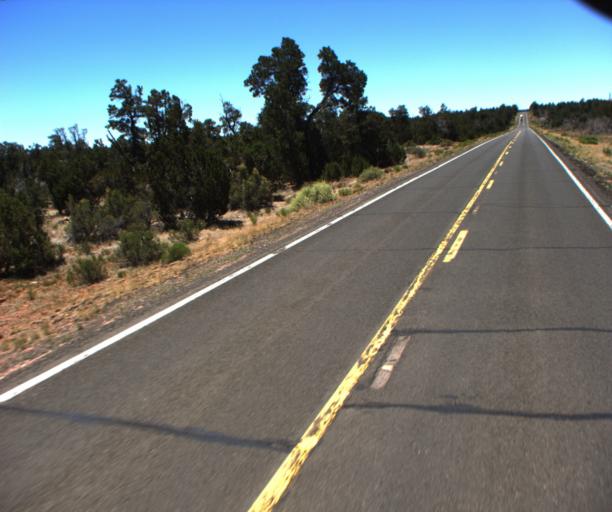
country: US
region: Arizona
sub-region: Coconino County
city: LeChee
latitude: 34.7108
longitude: -111.0950
